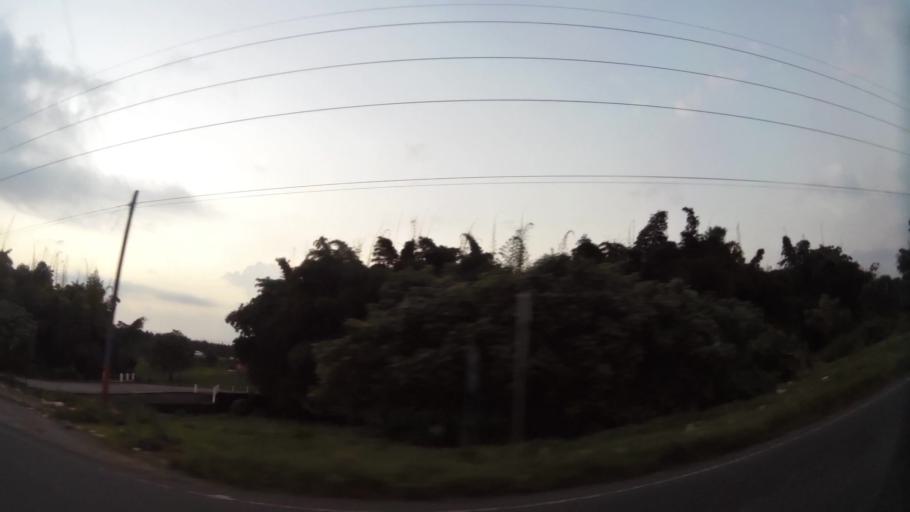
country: GT
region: Retalhuleu
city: San Felipe
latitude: 14.6162
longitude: -91.5994
